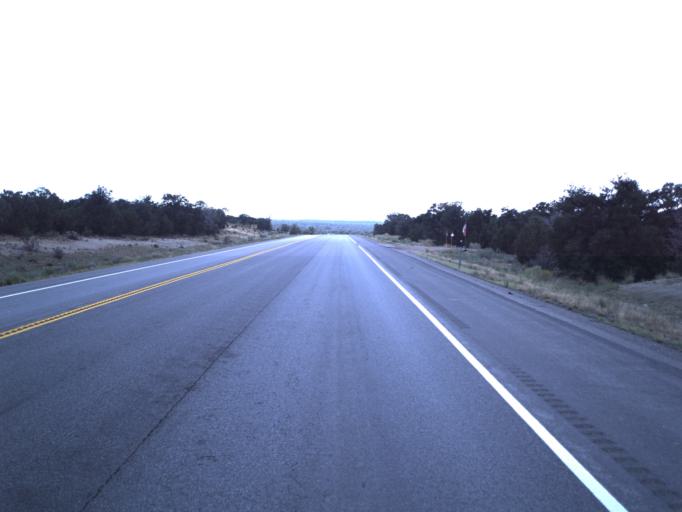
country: US
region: Utah
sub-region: Duchesne County
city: Duchesne
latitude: 40.1816
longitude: -110.6461
